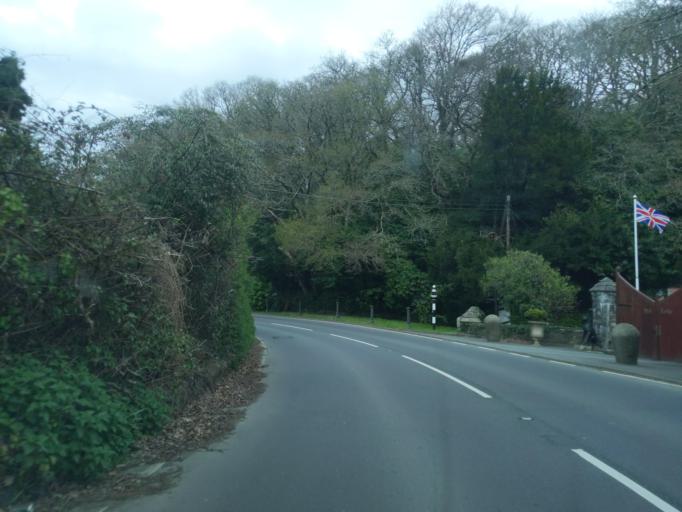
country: GB
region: England
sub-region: Devon
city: Great Torrington
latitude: 50.9449
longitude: -4.1358
